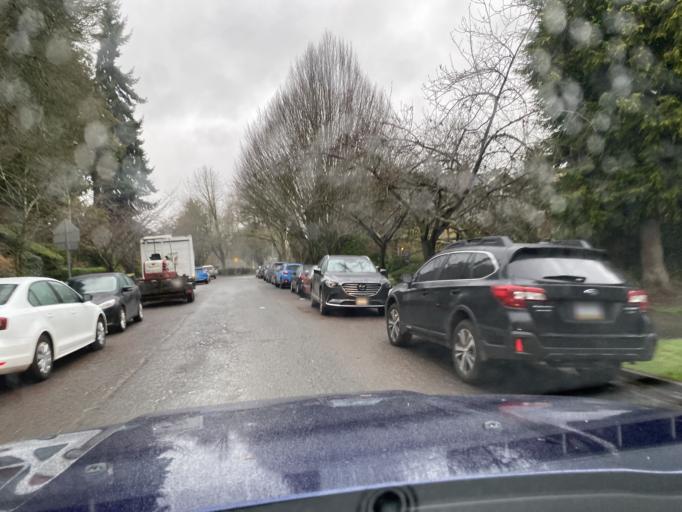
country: US
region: Washington
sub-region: King County
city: Seattle
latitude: 47.6279
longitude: -122.3087
